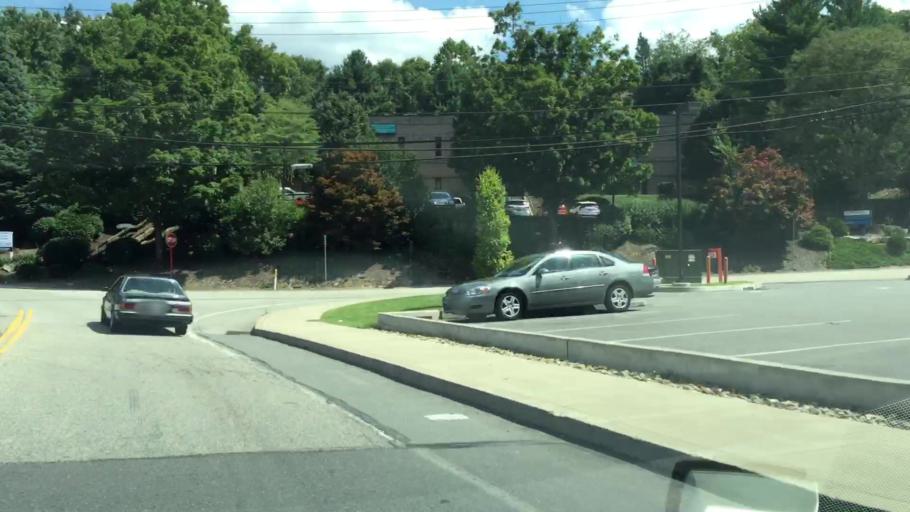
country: US
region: Pennsylvania
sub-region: Allegheny County
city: Upper Saint Clair
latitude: 40.3262
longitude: -80.0655
